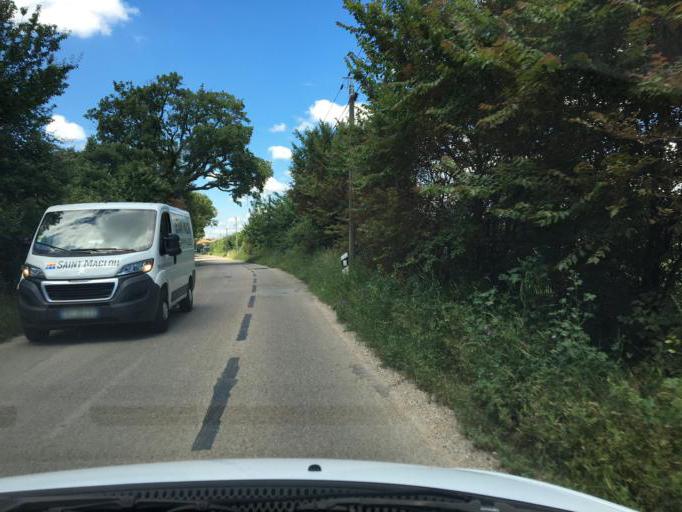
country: FR
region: Provence-Alpes-Cote d'Azur
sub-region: Departement du Vaucluse
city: Carpentras
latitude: 44.0398
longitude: 5.0559
